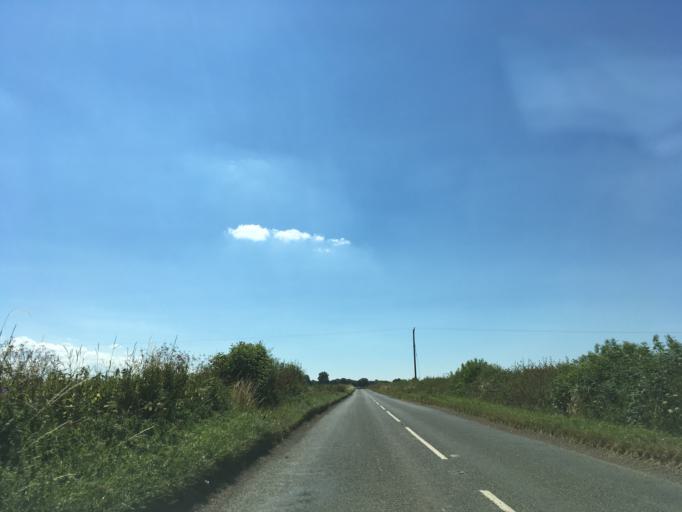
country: GB
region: England
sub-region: South Gloucestershire
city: Marshfield
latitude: 51.5130
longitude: -2.3212
